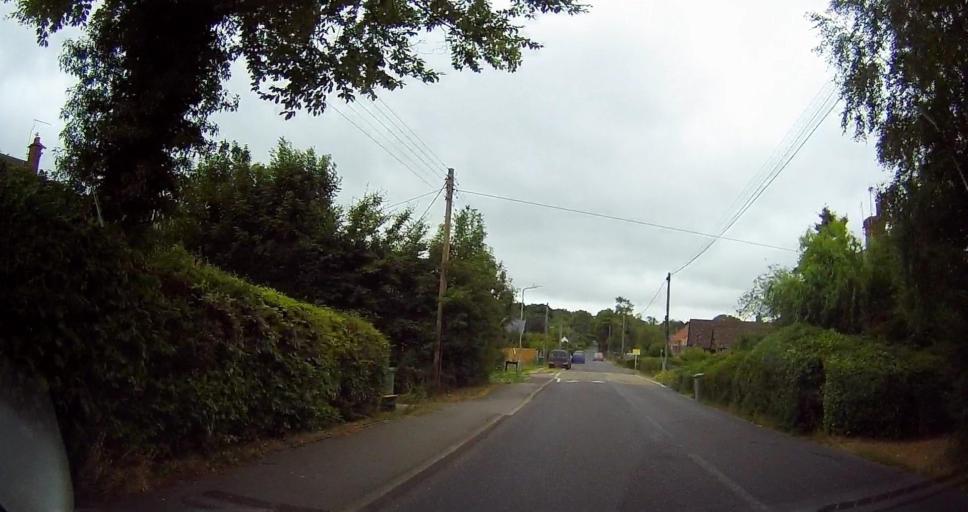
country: GB
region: England
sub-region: East Sussex
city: Wadhurst
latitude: 51.0917
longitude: 0.3870
